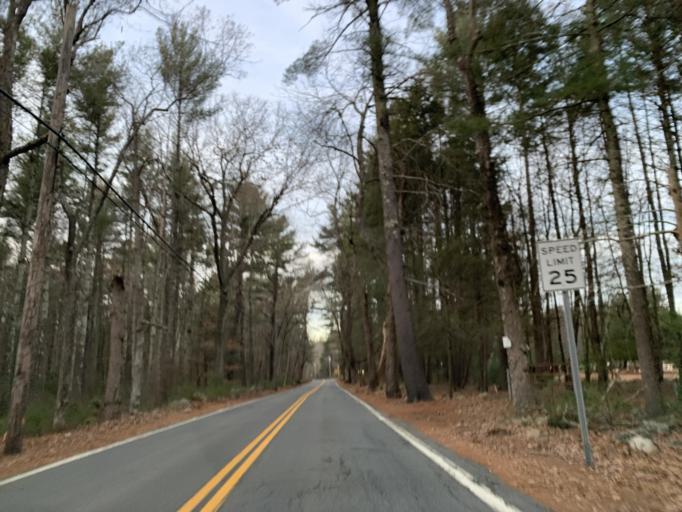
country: US
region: Rhode Island
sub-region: Providence County
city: Pascoag
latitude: 41.9294
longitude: -71.6999
